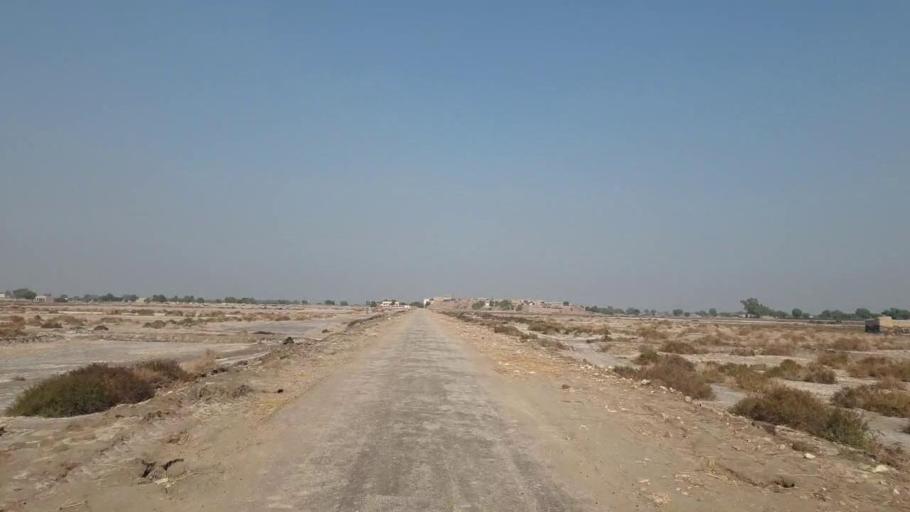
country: PK
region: Sindh
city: Sehwan
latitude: 26.4224
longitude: 67.7959
